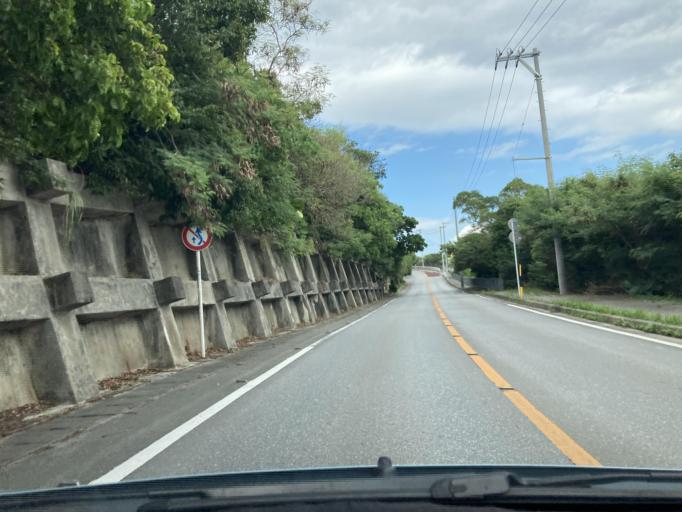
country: JP
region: Okinawa
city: Ginowan
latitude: 26.2644
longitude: 127.7850
